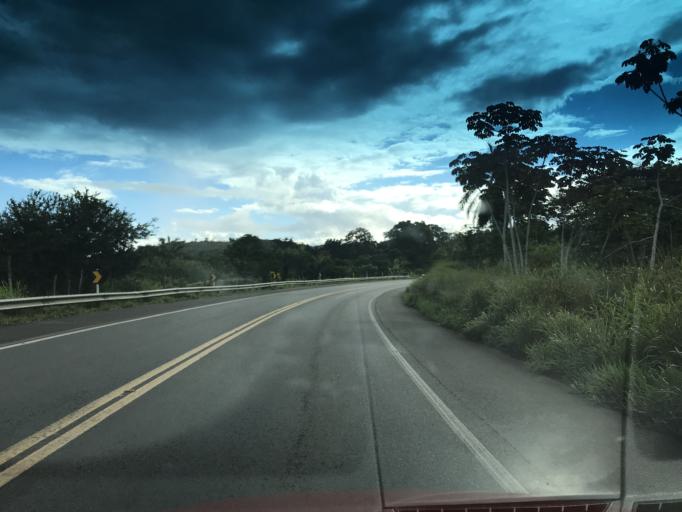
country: BR
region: Bahia
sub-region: Ibirapitanga
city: Ibirapitanga
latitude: -14.1516
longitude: -39.3438
